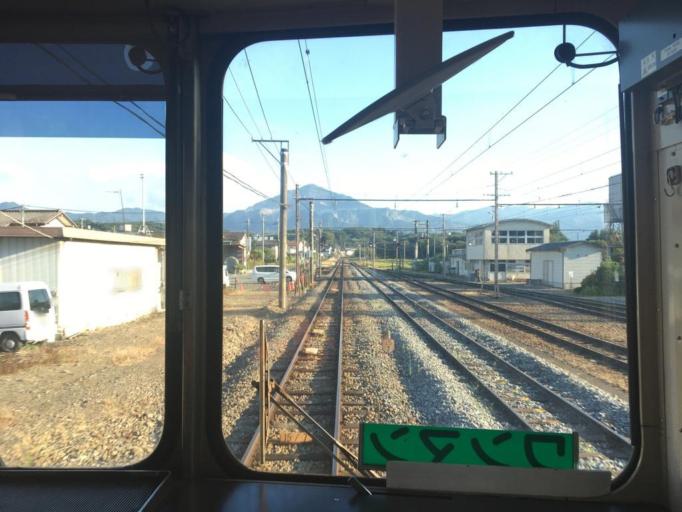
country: JP
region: Saitama
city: Chichibu
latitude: 36.0276
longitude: 139.0970
